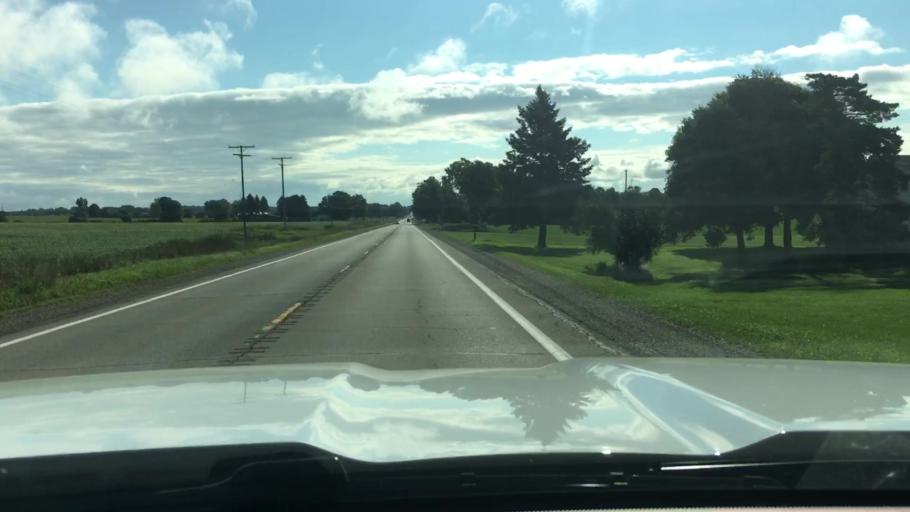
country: US
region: Michigan
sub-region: Tuscola County
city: Cass City
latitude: 43.6003
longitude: -83.2060
